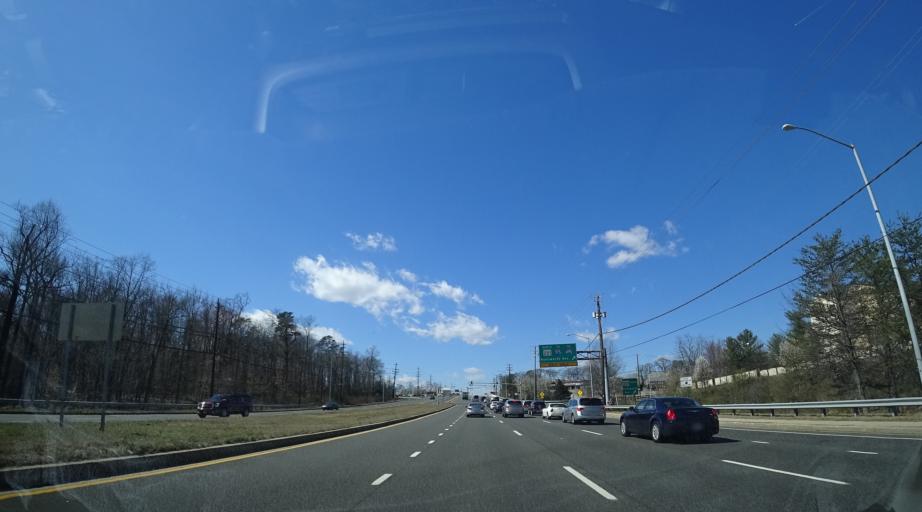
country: US
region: Maryland
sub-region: Prince George's County
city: Berwyn Heights
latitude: 38.9963
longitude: -76.8968
